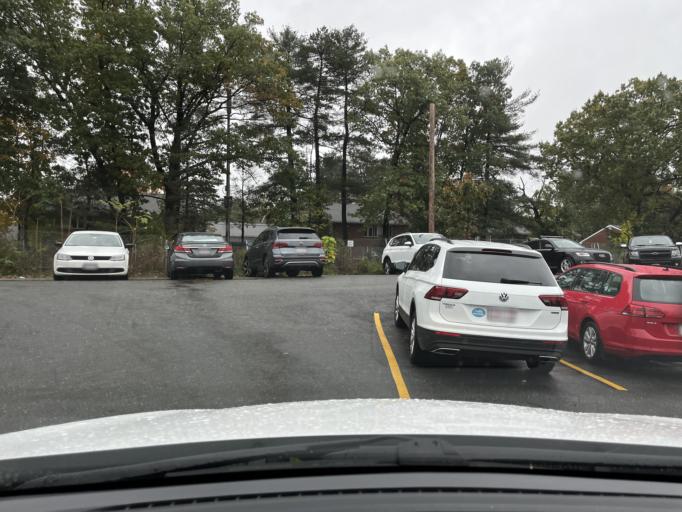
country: US
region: Massachusetts
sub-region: Norfolk County
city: Wellesley
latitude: 42.3005
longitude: -71.2902
